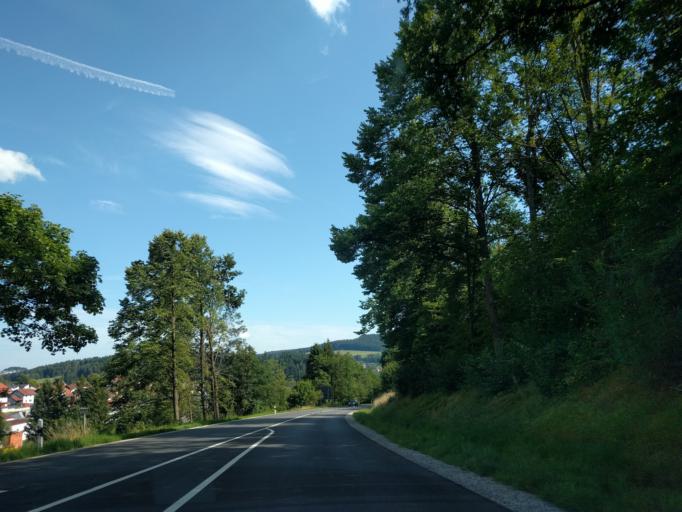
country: DE
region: Bavaria
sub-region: Lower Bavaria
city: Regen
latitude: 48.9823
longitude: 13.1347
